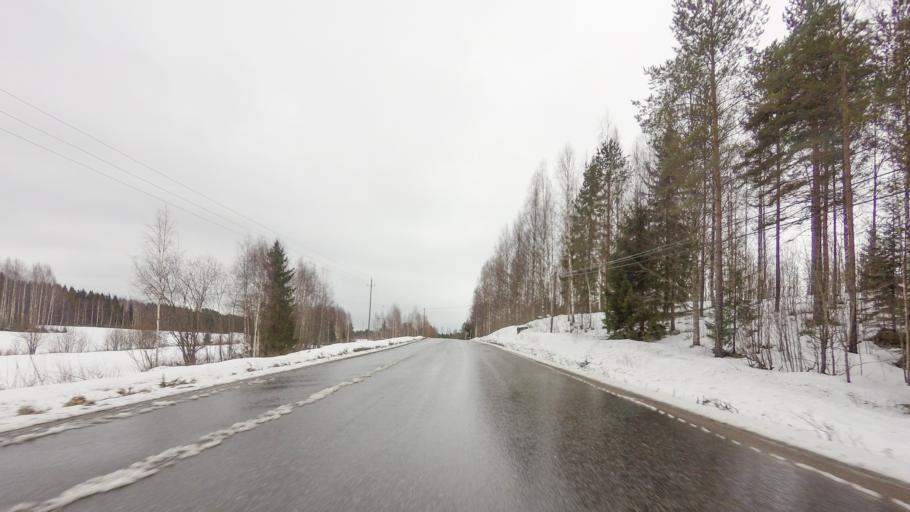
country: FI
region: Southern Savonia
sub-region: Savonlinna
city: Savonlinna
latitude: 61.9331
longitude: 28.8743
